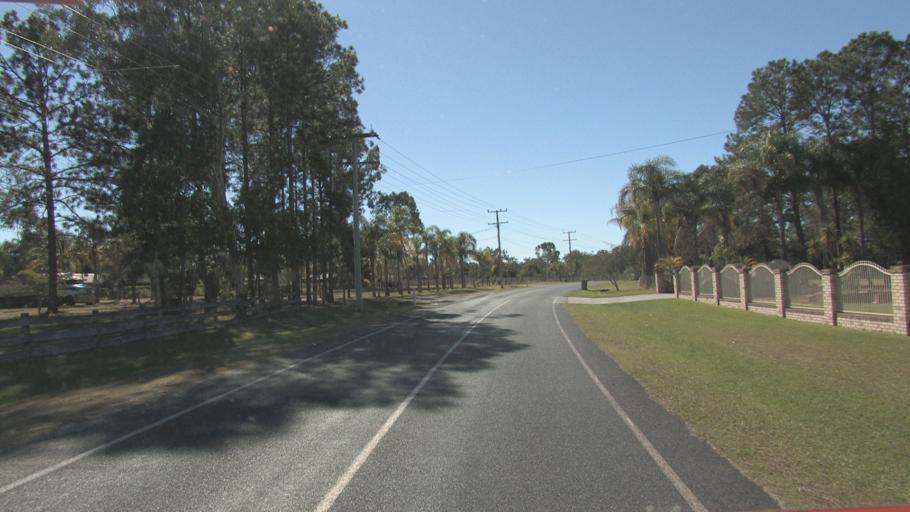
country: AU
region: Queensland
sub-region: Logan
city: Park Ridge South
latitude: -27.7251
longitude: 153.0534
